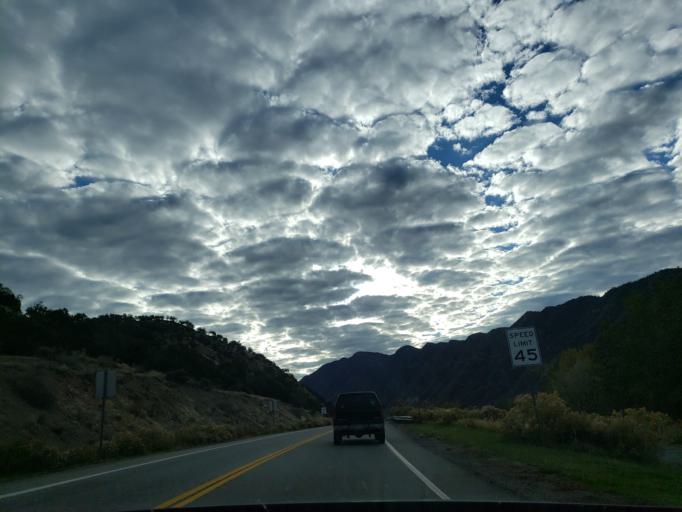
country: US
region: Colorado
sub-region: Garfield County
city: New Castle
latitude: 39.5712
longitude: -107.5249
